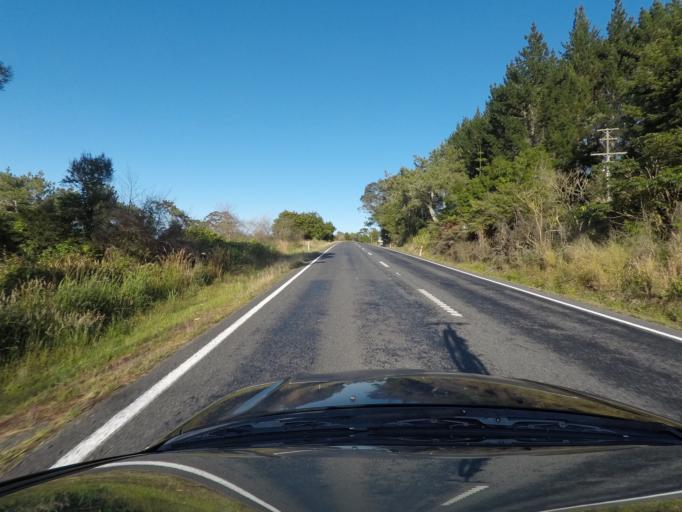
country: NZ
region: Northland
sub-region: Far North District
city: Kawakawa
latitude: -35.4945
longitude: 174.1407
